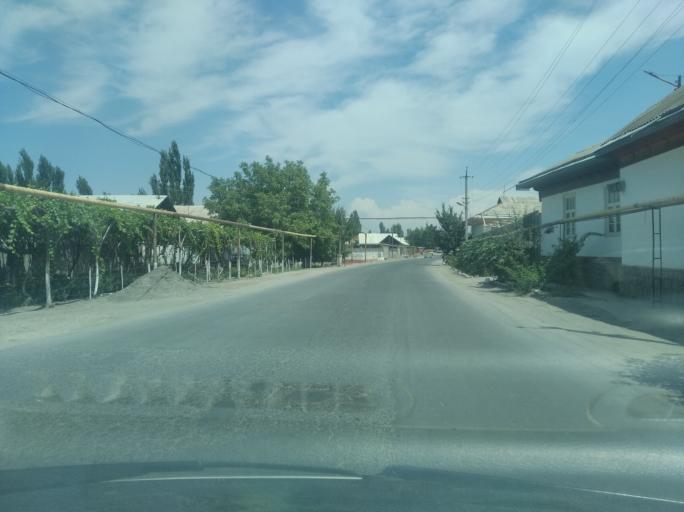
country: UZ
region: Andijon
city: Khujaobod
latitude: 40.6269
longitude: 72.4503
